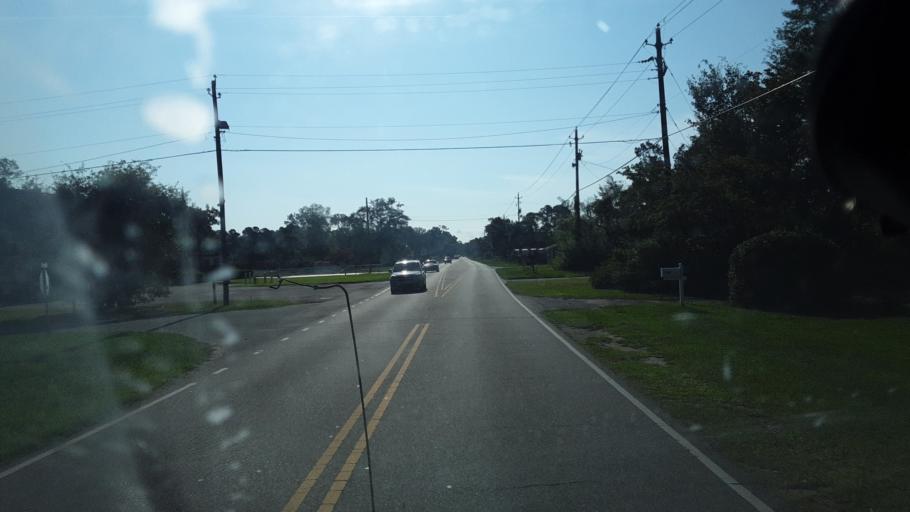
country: US
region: North Carolina
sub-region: Brunswick County
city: Leland
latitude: 34.2487
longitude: -78.0290
